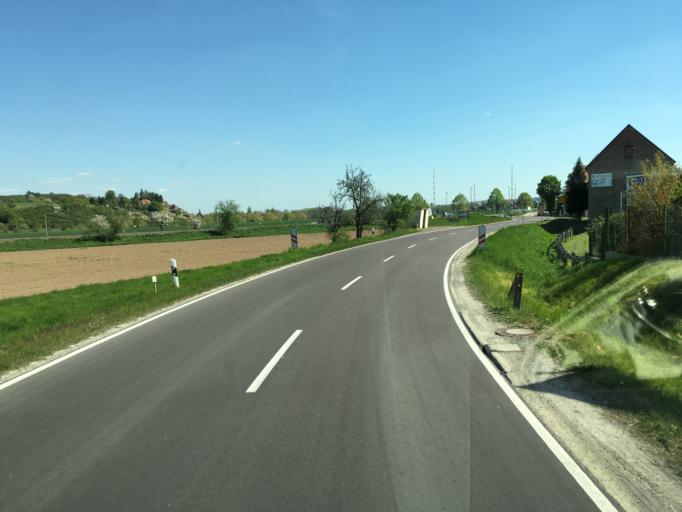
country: DE
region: Saxony-Anhalt
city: Freyburg
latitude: 51.1819
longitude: 11.7797
